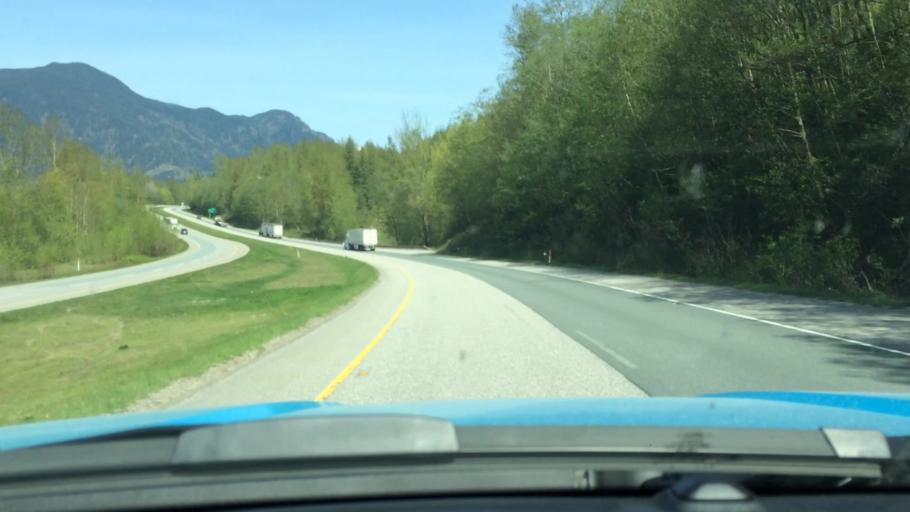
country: CA
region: British Columbia
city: Agassiz
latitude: 49.2751
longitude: -121.6722
